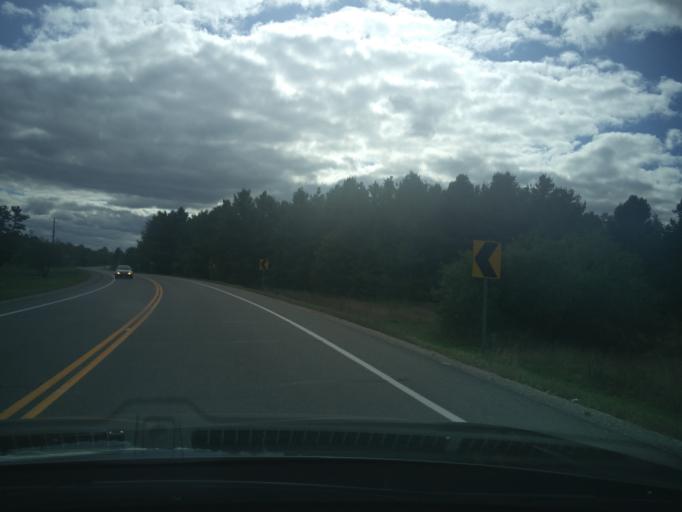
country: CA
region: Ontario
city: Carleton Place
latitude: 45.0238
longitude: -76.0798
